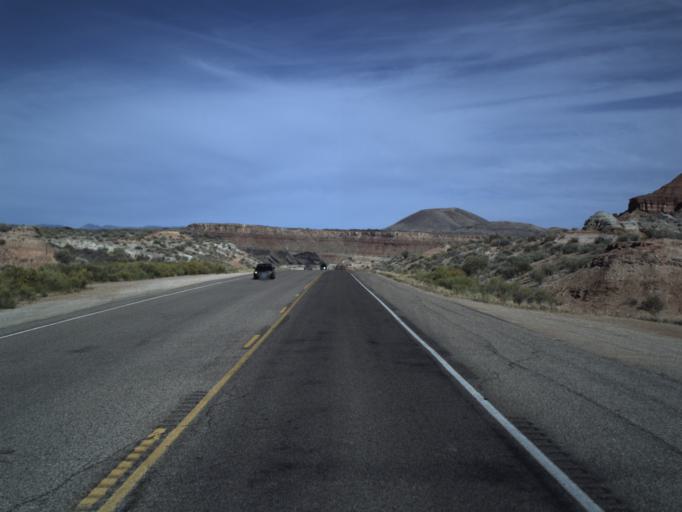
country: US
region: Utah
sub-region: Washington County
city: Hildale
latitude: 37.1674
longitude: -113.0641
